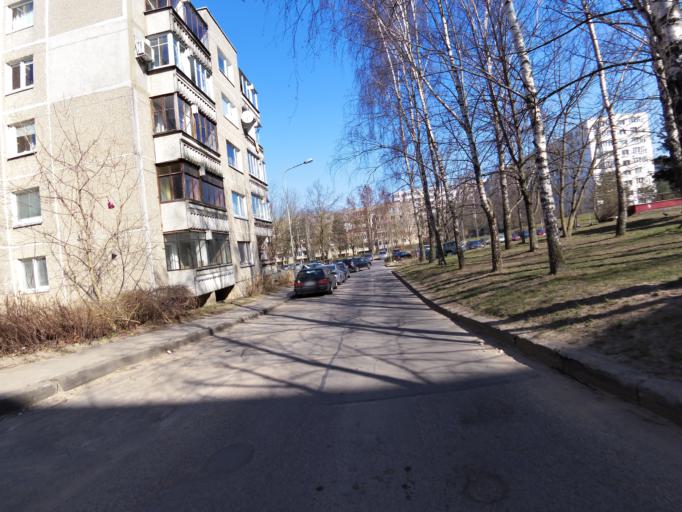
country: LT
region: Vilnius County
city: Justiniskes
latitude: 54.7207
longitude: 25.2203
